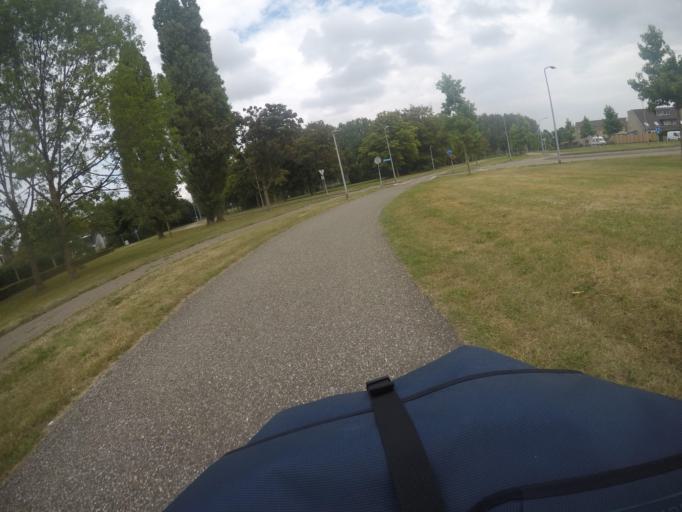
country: NL
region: Flevoland
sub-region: Gemeente Almere
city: Almere Stad
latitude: 52.3737
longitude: 5.1892
